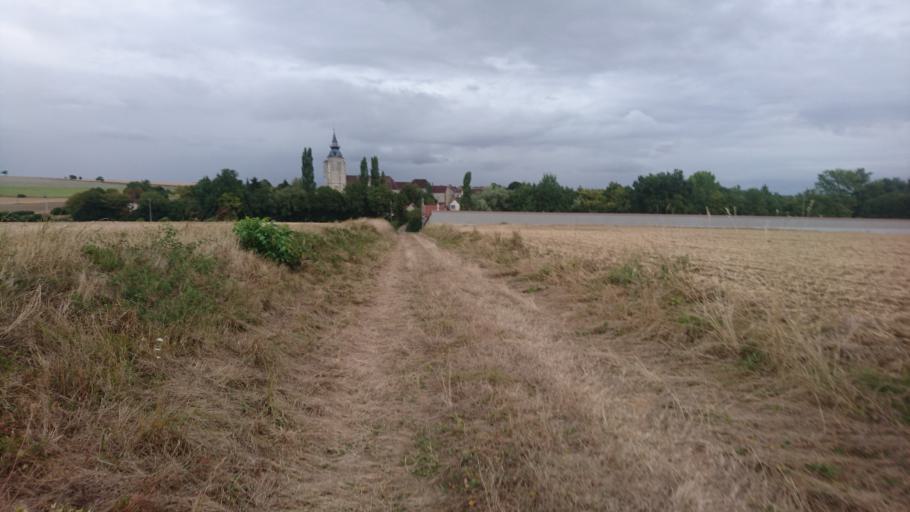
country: FR
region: Bourgogne
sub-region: Departement de l'Yonne
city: Aillant-sur-Tholon
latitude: 47.8620
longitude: 3.3919
